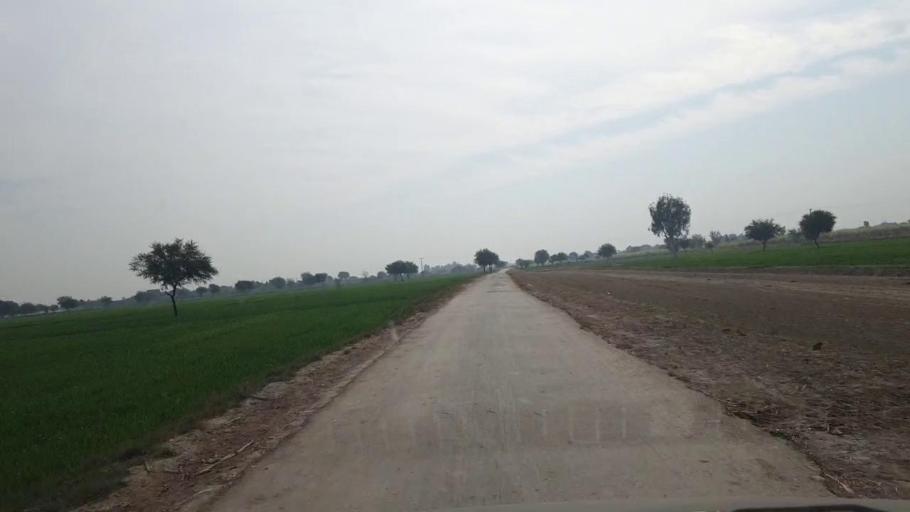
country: PK
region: Sindh
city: Shahdadpur
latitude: 25.9524
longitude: 68.6999
